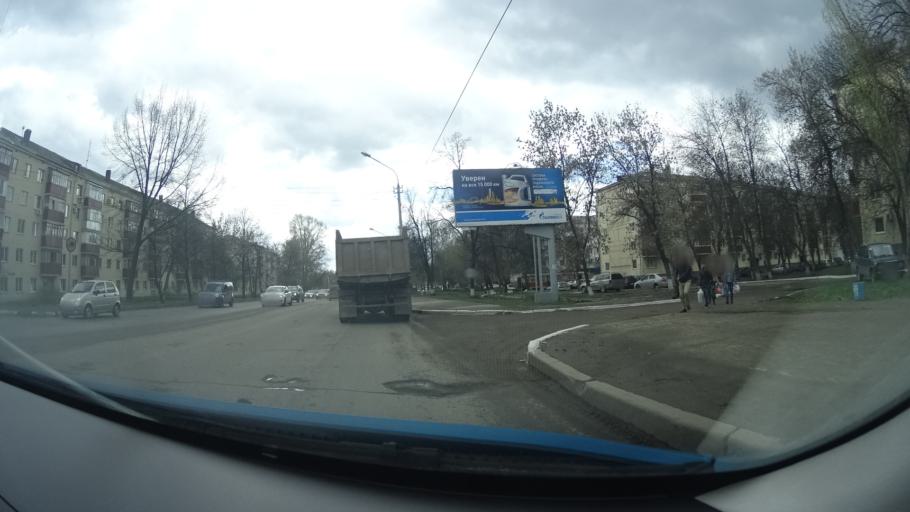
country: RU
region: Bashkortostan
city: Ufa
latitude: 54.8127
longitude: 56.0891
